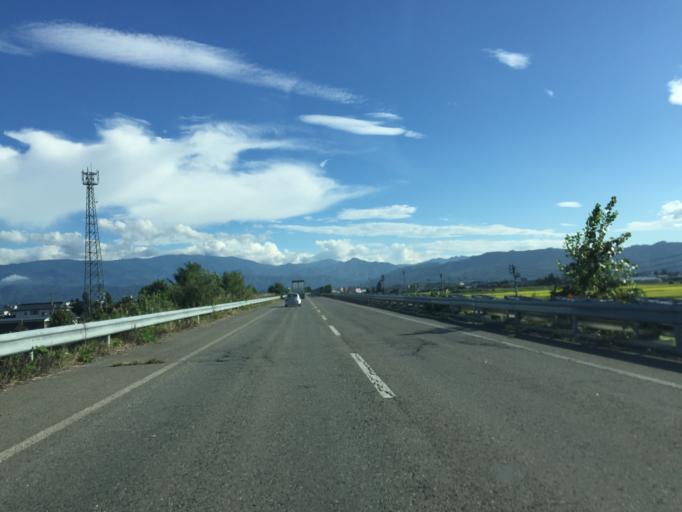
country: JP
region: Yamagata
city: Yonezawa
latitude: 37.9431
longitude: 140.1116
